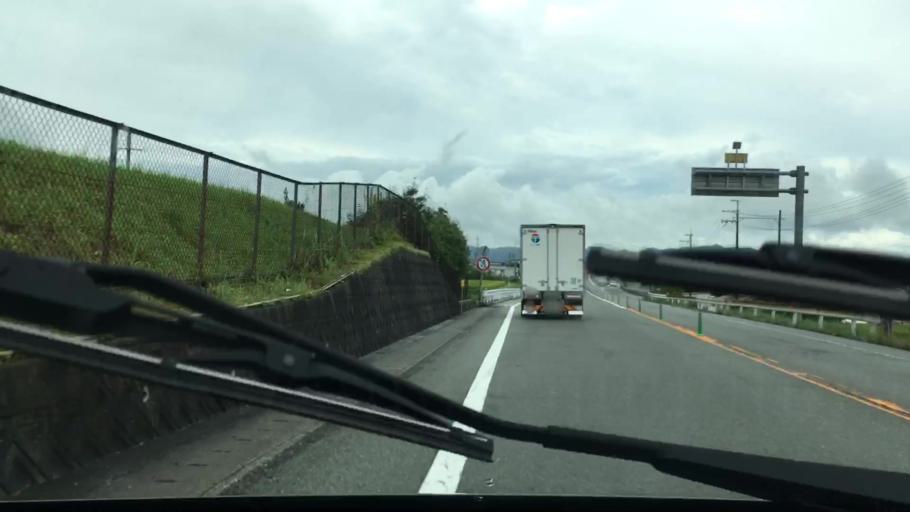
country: JP
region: Hyogo
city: Himeji
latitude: 34.9587
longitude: 134.7698
